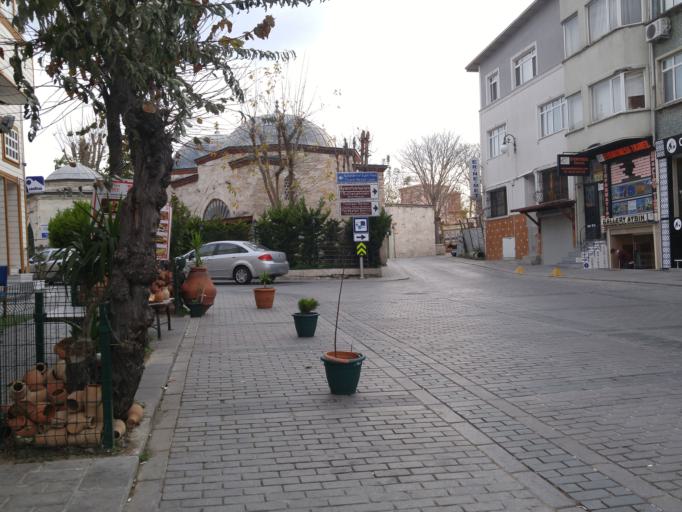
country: TR
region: Istanbul
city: Eminoenue
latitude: 41.0040
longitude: 28.9763
